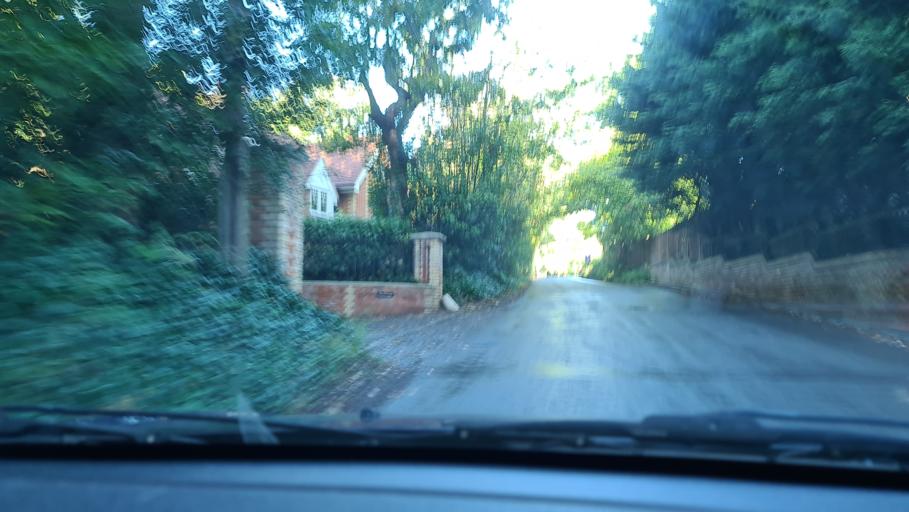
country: GB
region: England
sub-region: Hertfordshire
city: Chorleywood
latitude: 51.6435
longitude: -0.5222
